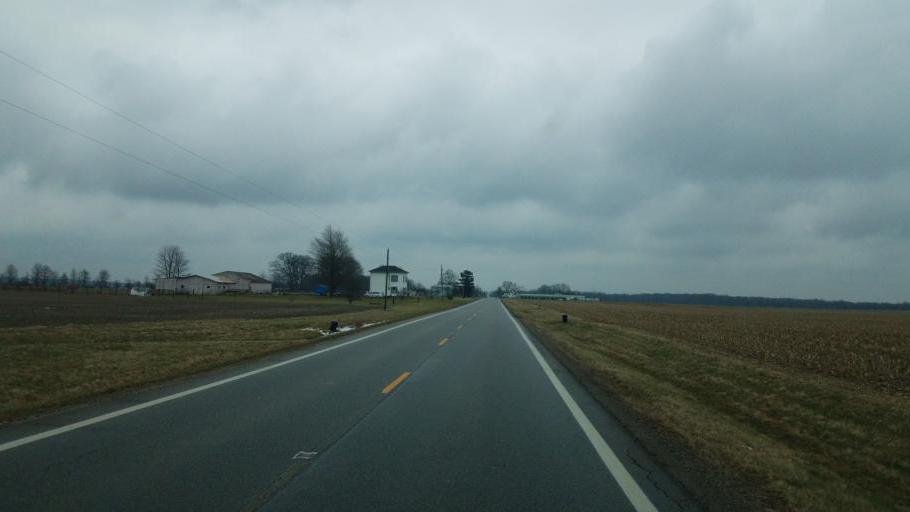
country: US
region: Ohio
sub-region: Delaware County
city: Ashley
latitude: 40.4080
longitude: -82.9307
